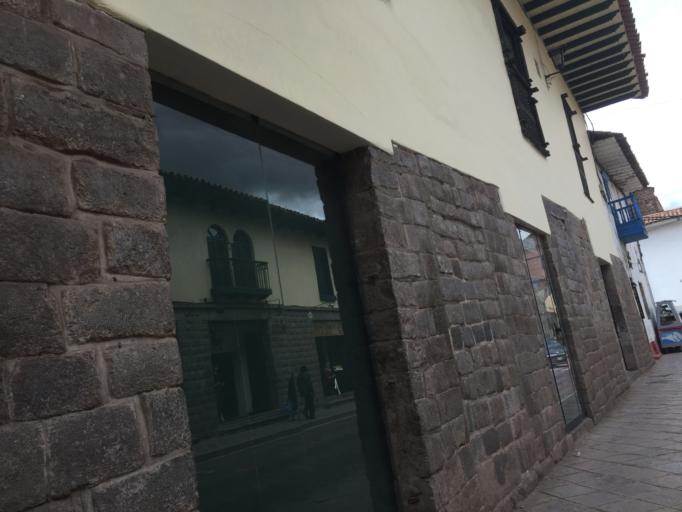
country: PE
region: Cusco
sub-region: Provincia de Cusco
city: Cusco
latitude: -13.5172
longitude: -71.9770
